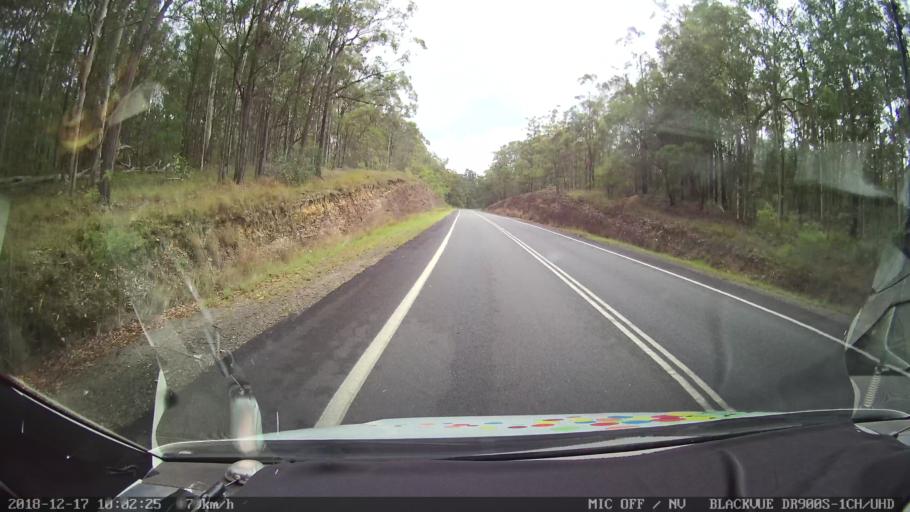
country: AU
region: New South Wales
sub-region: Tenterfield Municipality
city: Carrolls Creek
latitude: -28.9026
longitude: 152.4515
